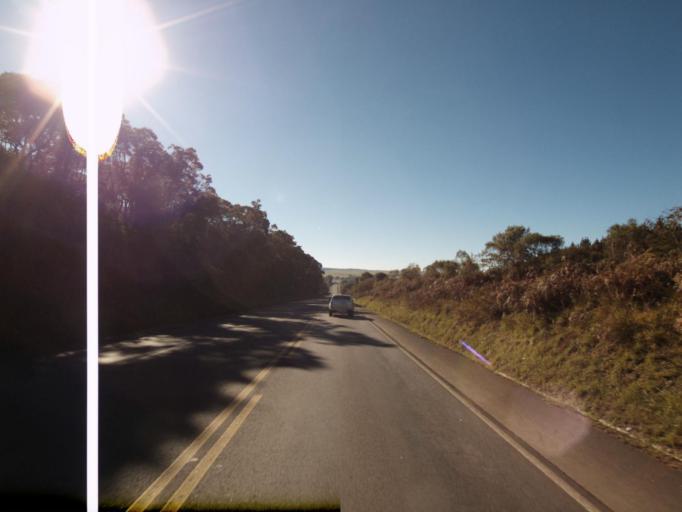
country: BR
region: Santa Catarina
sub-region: Concordia
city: Concordia
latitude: -26.9203
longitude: -51.9382
